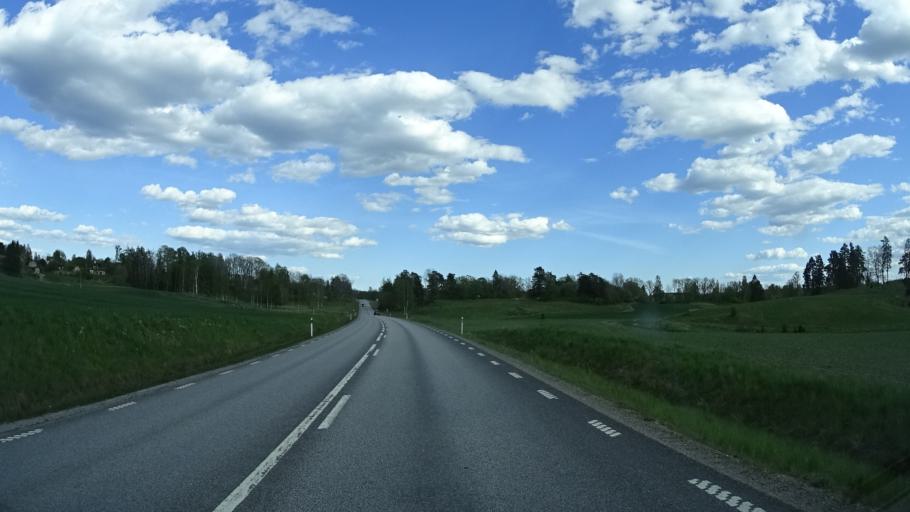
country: SE
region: OErebro
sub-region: Lindesbergs Kommun
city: Lindesberg
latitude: 59.5301
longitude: 15.2727
